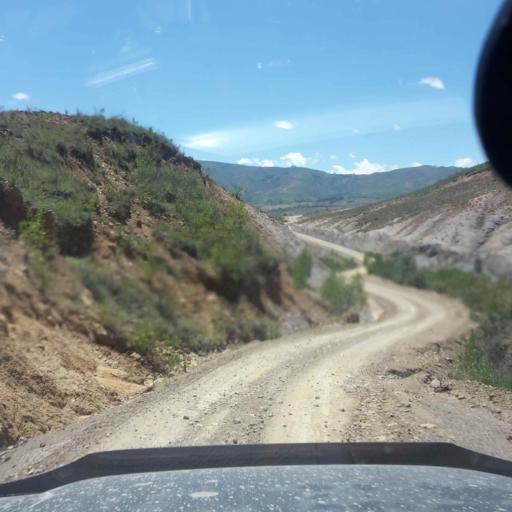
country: BO
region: Cochabamba
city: Totora
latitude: -17.7744
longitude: -65.2693
